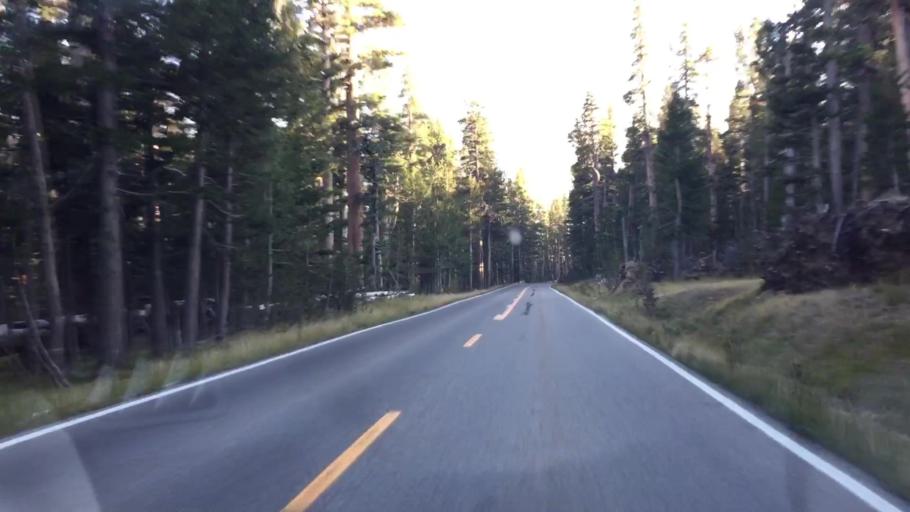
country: US
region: California
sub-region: Mariposa County
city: Yosemite Valley
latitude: 37.8953
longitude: -119.2599
